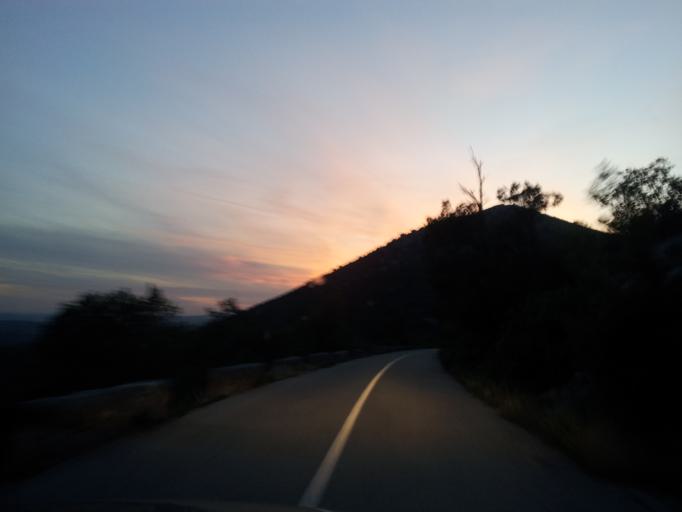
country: HR
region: Zadarska
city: Obrovac
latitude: 44.2374
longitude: 15.6706
